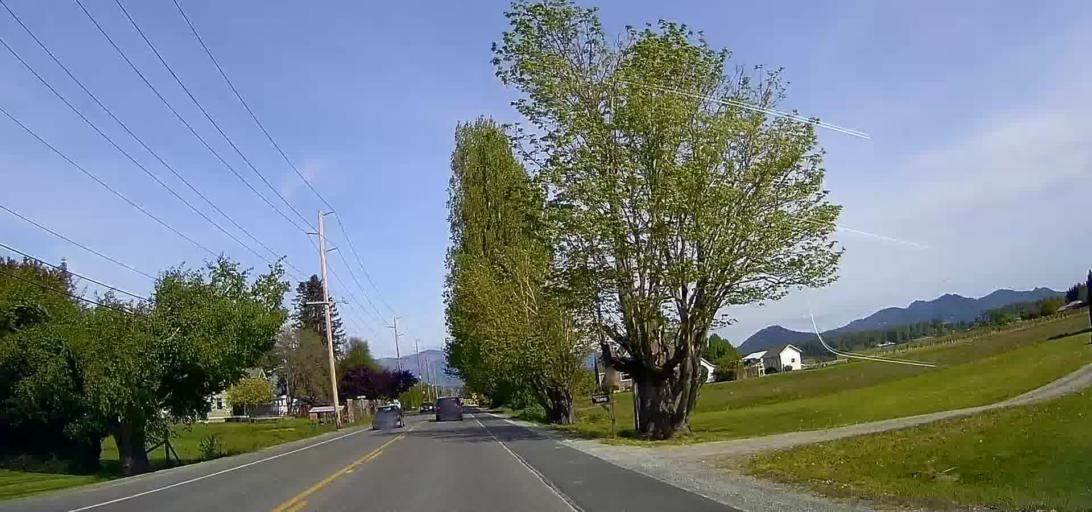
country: US
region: Washington
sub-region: Skagit County
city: Mount Vernon
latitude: 48.4209
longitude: -122.3892
